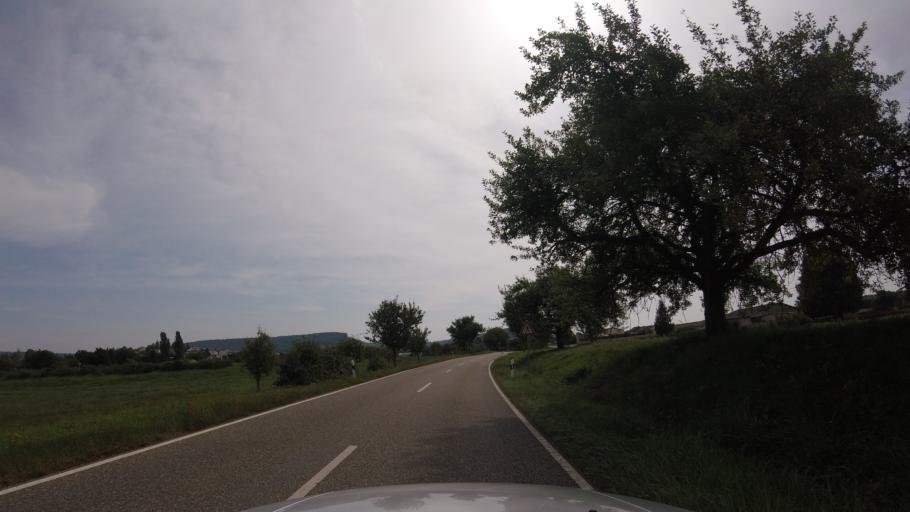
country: DE
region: Baden-Wuerttemberg
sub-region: Regierungsbezirk Stuttgart
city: Grossbottwar
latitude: 49.0069
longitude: 9.2812
